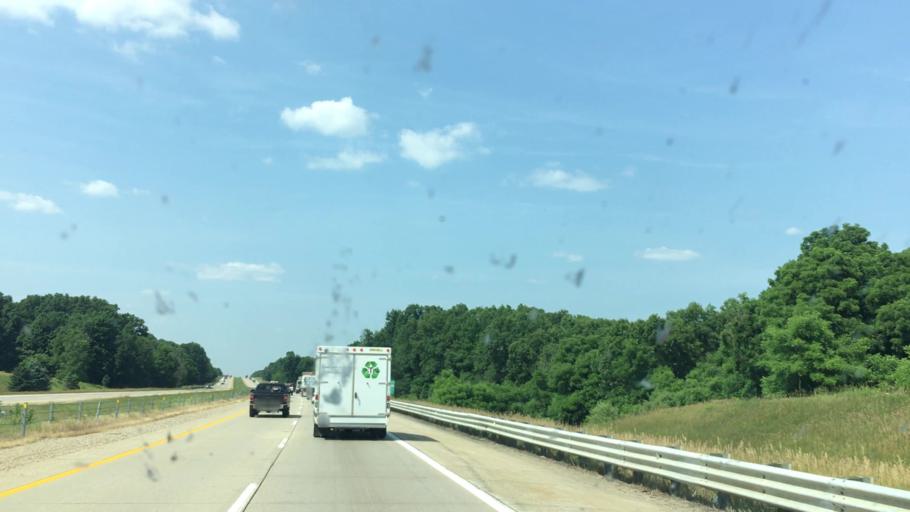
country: US
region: Michigan
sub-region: Allegan County
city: Plainwell
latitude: 42.4935
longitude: -85.6516
